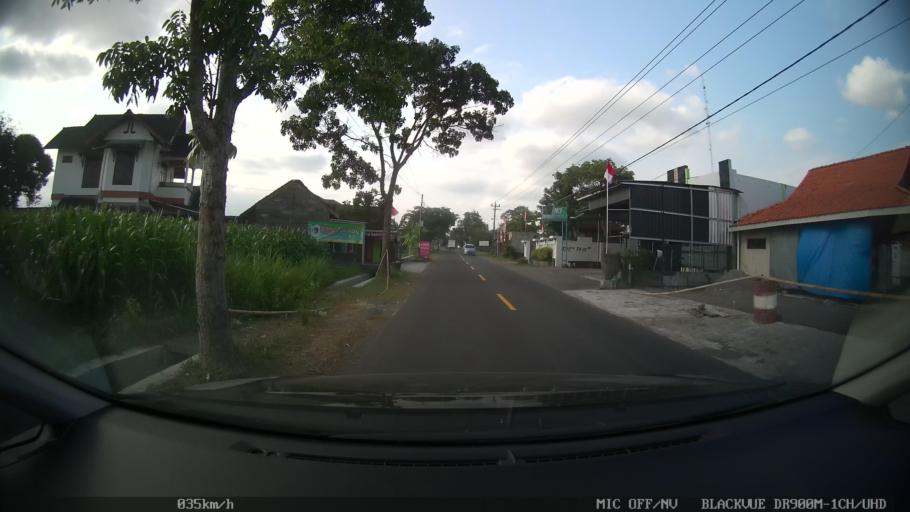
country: ID
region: Central Java
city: Candi Prambanan
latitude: -7.7216
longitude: 110.4726
